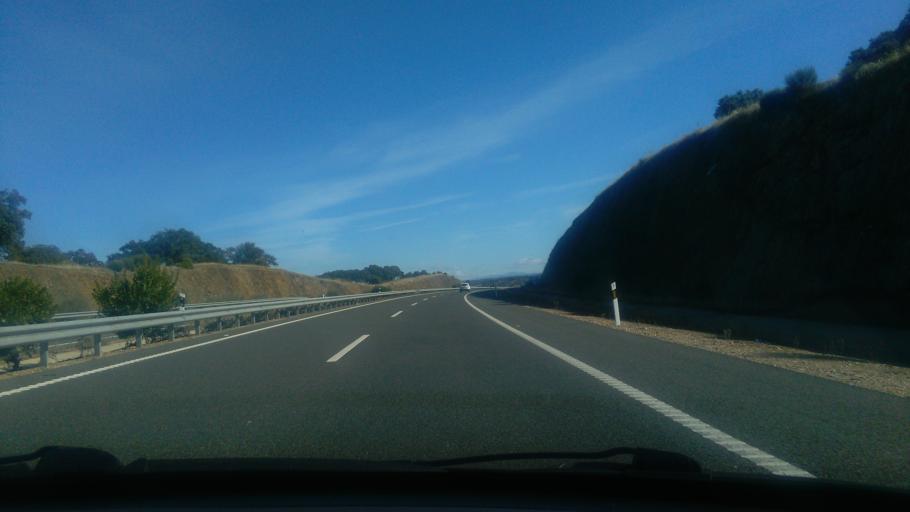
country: ES
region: Extremadura
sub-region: Provincia de Caceres
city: Plasenzuela
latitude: 39.4400
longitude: -6.0749
